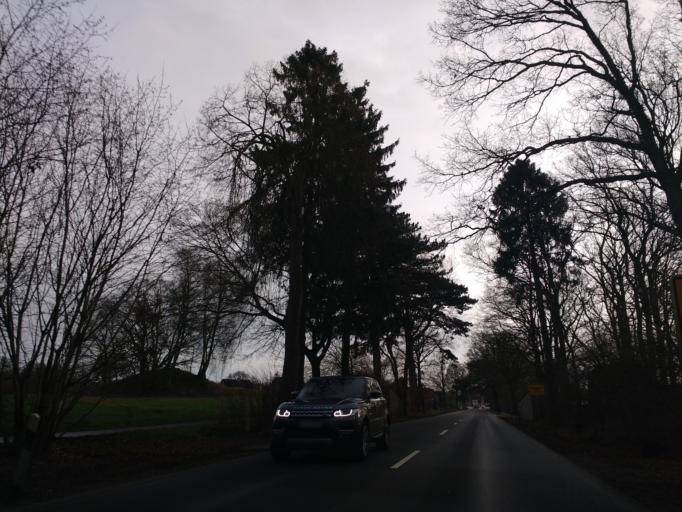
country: DE
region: Schleswig-Holstein
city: Ratekau
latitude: 53.9930
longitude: 10.7091
